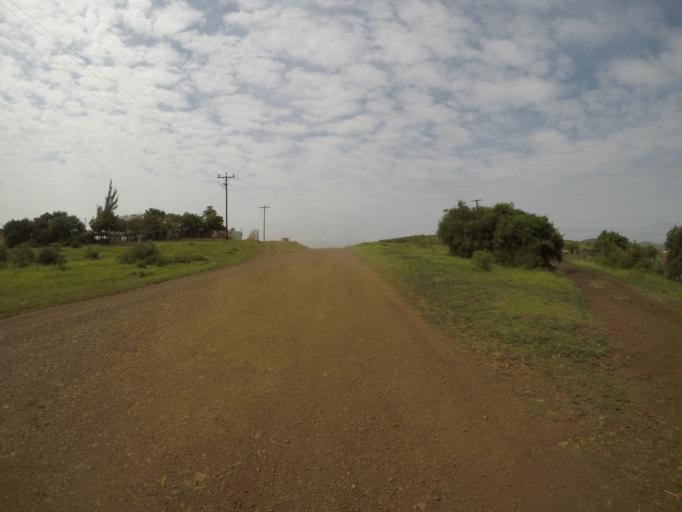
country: ZA
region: KwaZulu-Natal
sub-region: uThungulu District Municipality
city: Empangeni
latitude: -28.6186
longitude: 31.9032
